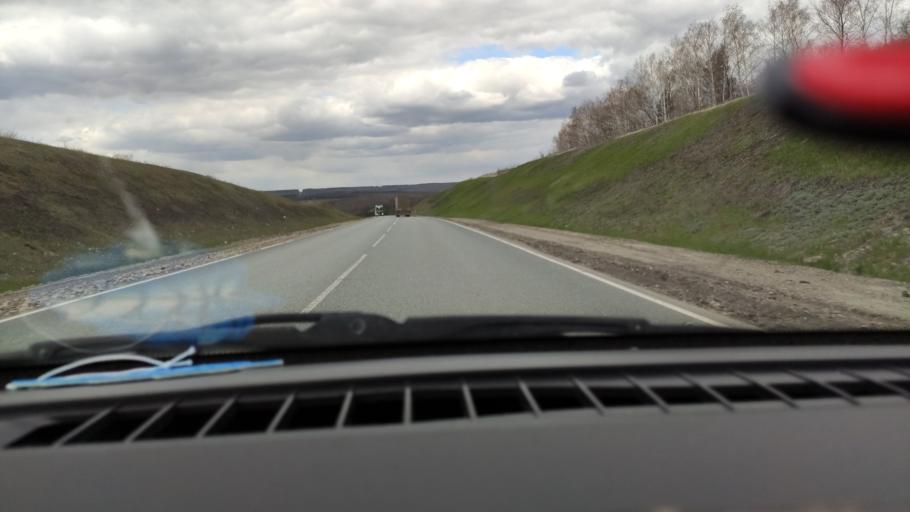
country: RU
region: Saratov
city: Tersa
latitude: 52.1037
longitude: 47.4902
